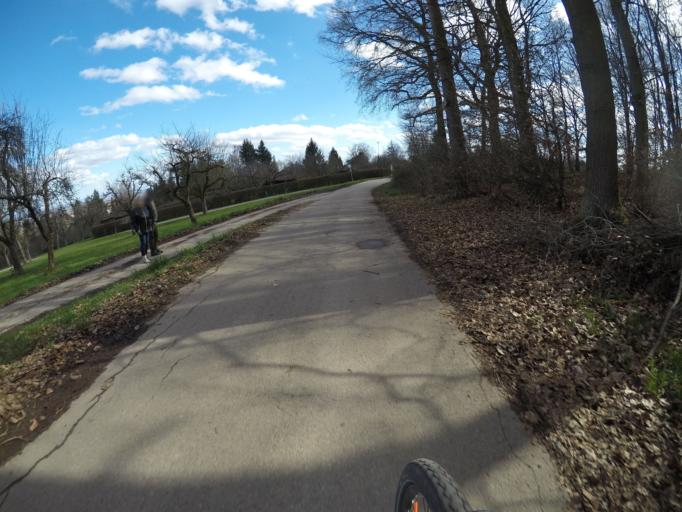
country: DE
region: Baden-Wuerttemberg
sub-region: Regierungsbezirk Stuttgart
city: Leinfelden-Echterdingen
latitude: 48.6753
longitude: 9.1579
